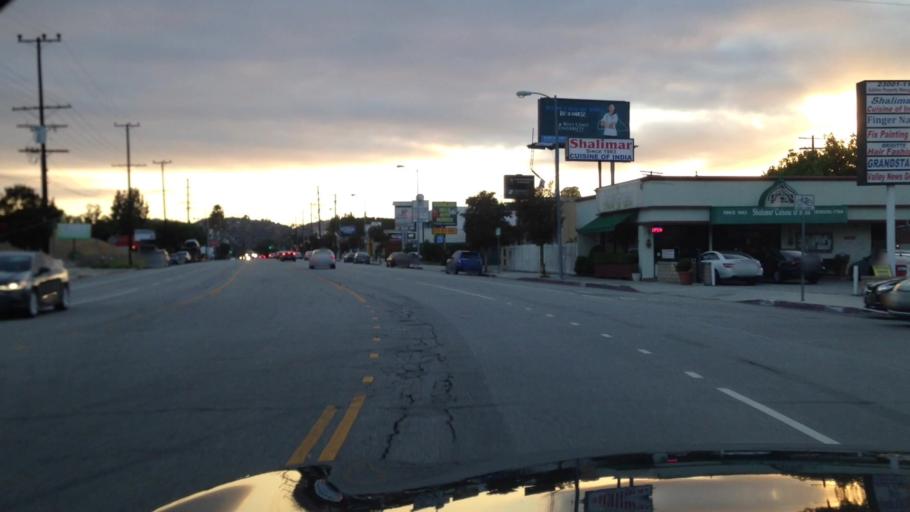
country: US
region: California
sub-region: Los Angeles County
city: Calabasas
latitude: 34.1650
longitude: -118.6267
